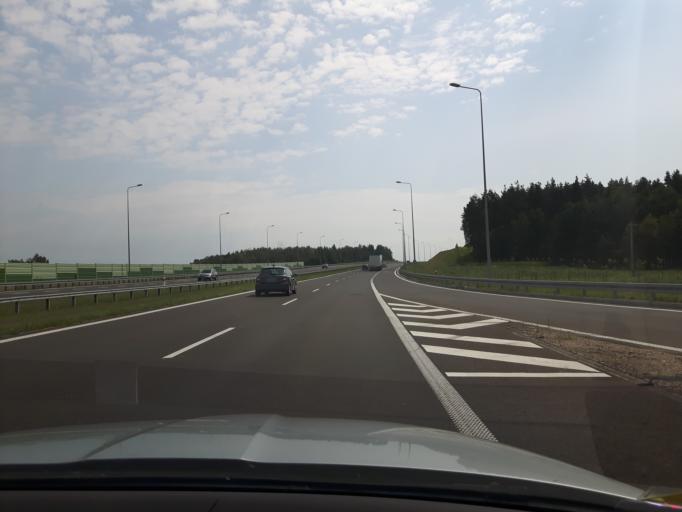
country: PL
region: Warmian-Masurian Voivodeship
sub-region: Powiat nidzicki
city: Nidzica
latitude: 53.3718
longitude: 20.3846
